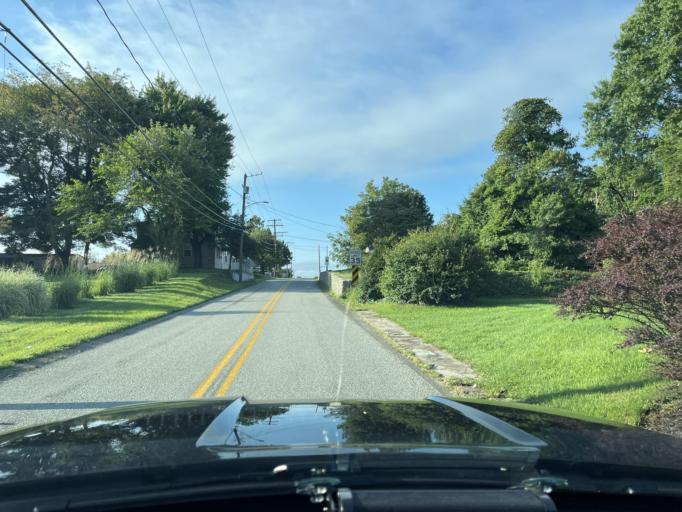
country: US
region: Pennsylvania
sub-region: Fayette County
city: Leith-Hatfield
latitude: 39.8814
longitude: -79.7270
